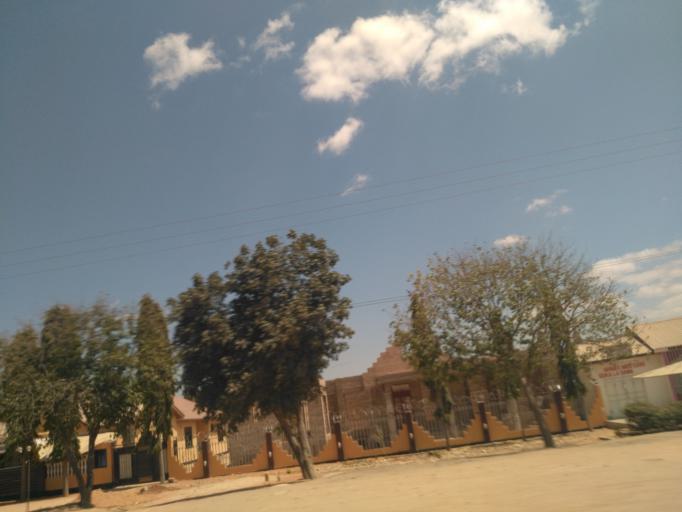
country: TZ
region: Dodoma
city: Kisasa
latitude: -6.1703
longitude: 35.7736
